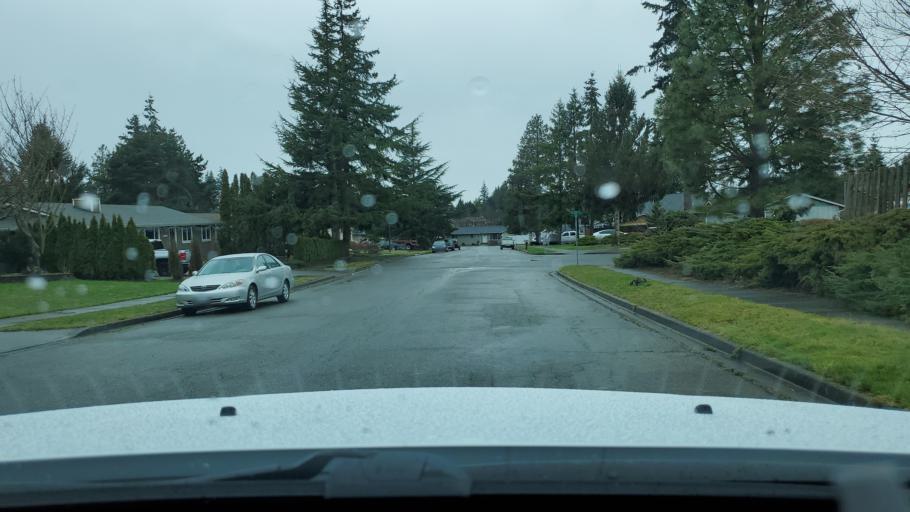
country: US
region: Washington
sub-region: Skagit County
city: Mount Vernon
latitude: 48.4415
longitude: -122.3150
